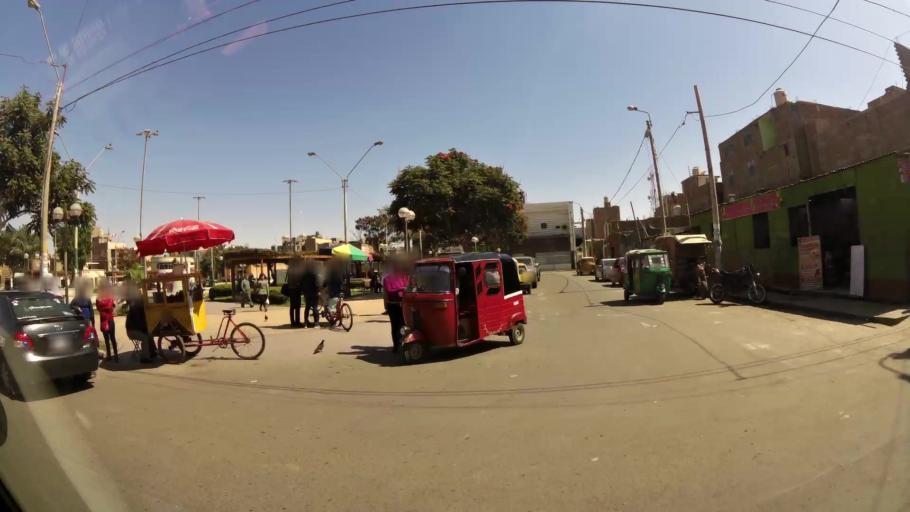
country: PE
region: Ica
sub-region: Provincia de Ica
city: Ica
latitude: -14.0666
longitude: -75.7260
